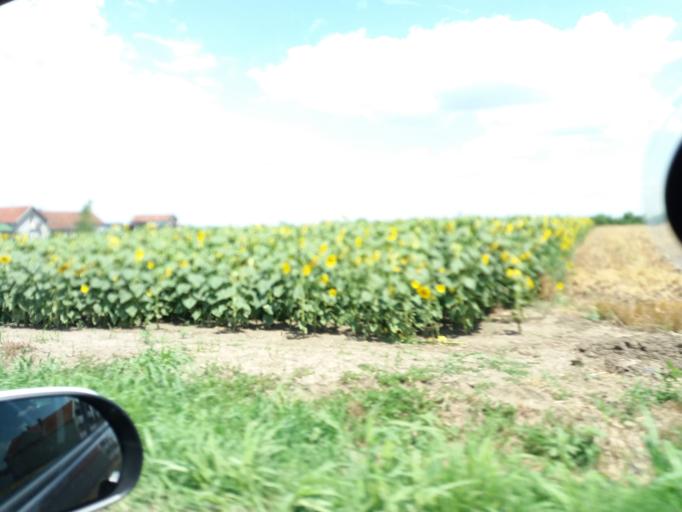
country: RS
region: Autonomna Pokrajina Vojvodina
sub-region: Sremski Okrug
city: Pecinci
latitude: 44.8516
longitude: 19.9614
